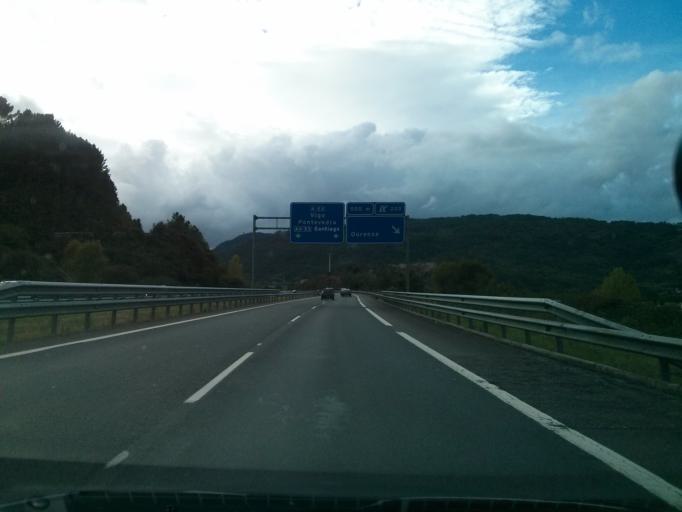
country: ES
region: Galicia
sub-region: Provincia de Ourense
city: Ourense
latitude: 42.3466
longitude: -7.9070
